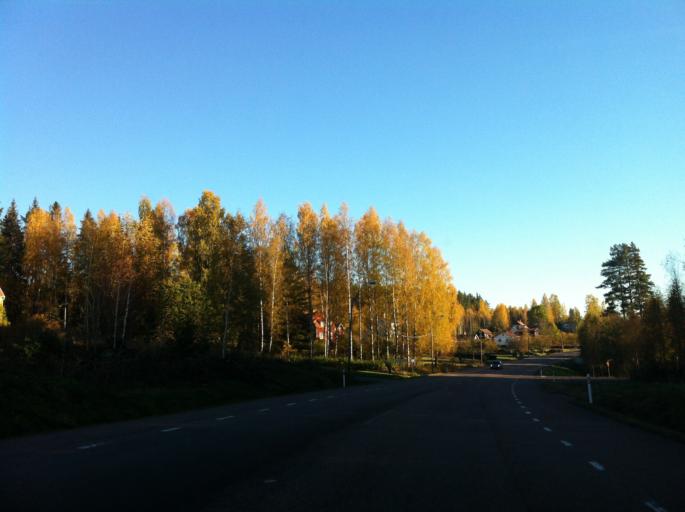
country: SE
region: Dalarna
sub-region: Faluns Kommun
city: Grycksbo
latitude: 60.7000
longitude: 15.4782
